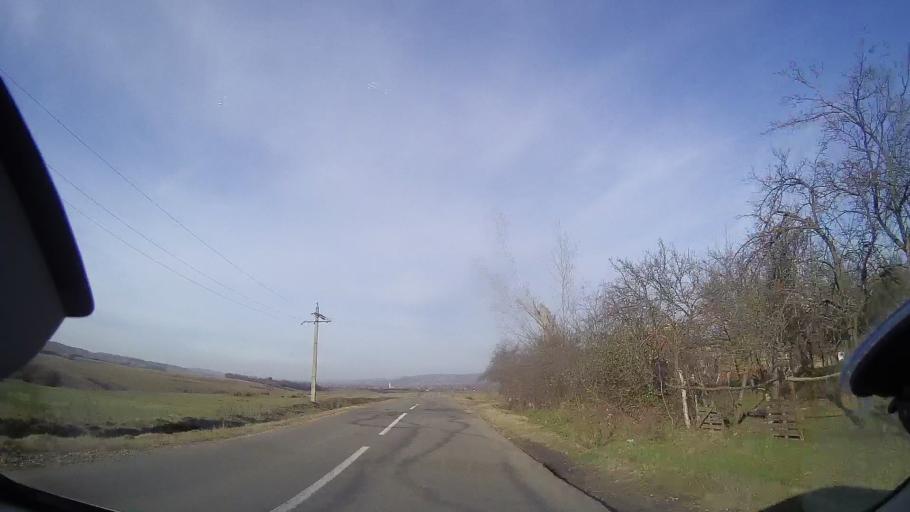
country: RO
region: Bihor
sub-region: Comuna Brusturi
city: Brusturi
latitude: 47.1297
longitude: 22.2705
